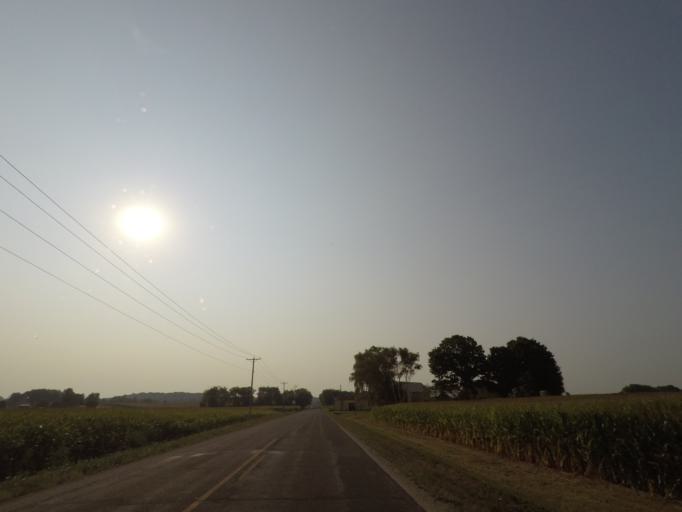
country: US
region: Wisconsin
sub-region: Dane County
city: Cottage Grove
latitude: 43.0500
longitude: -89.2430
